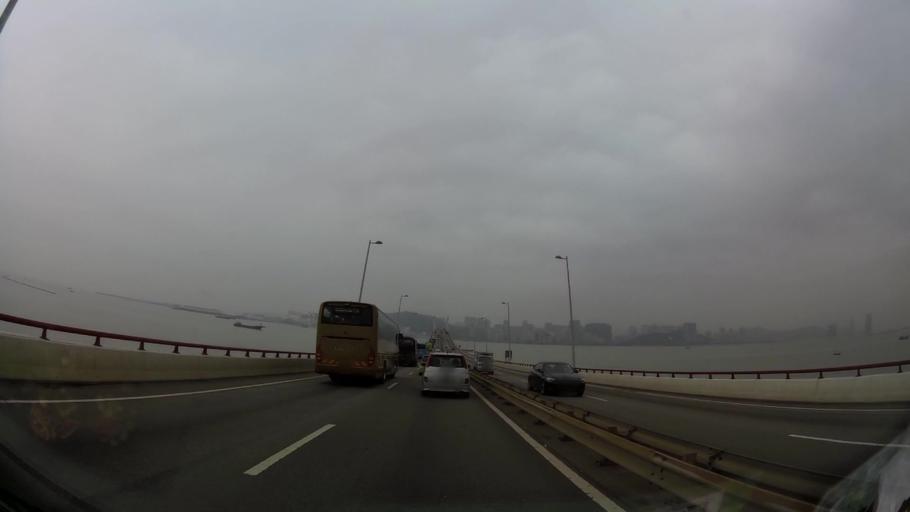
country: MO
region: Macau
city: Macau
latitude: 22.1872
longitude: 113.5634
